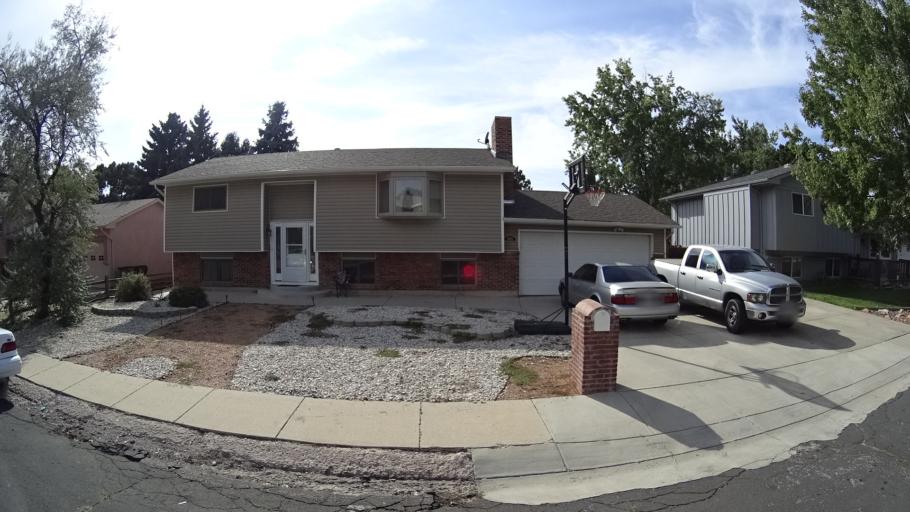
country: US
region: Colorado
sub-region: El Paso County
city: Cimarron Hills
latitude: 38.8967
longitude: -104.7696
